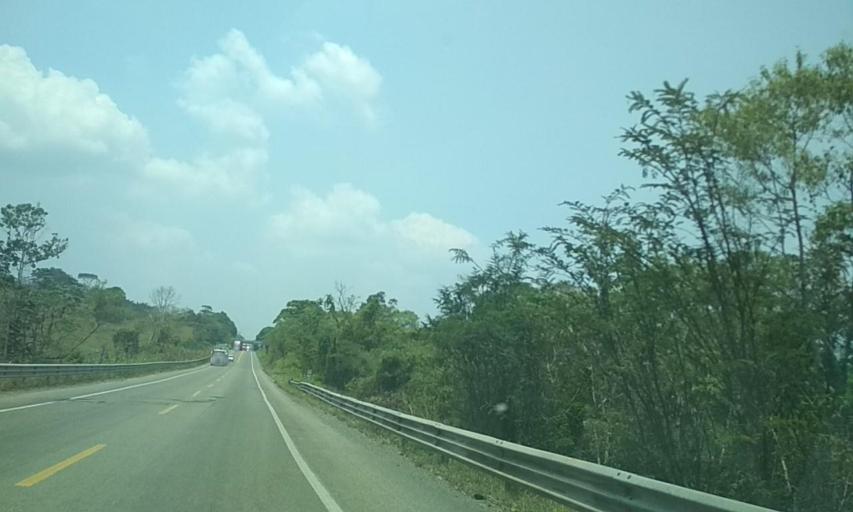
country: MX
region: Tabasco
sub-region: Huimanguillo
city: Francisco Rueda
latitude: 17.6709
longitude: -93.8704
